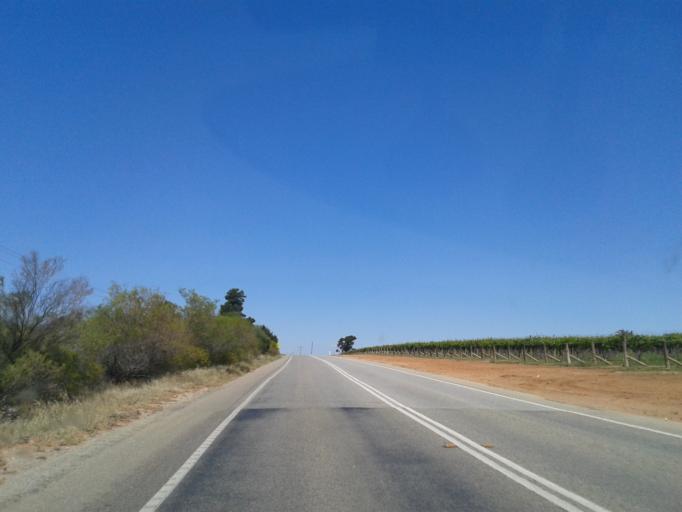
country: AU
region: Victoria
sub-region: Mildura Shire
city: Ouyen
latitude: -34.6055
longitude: 142.7914
